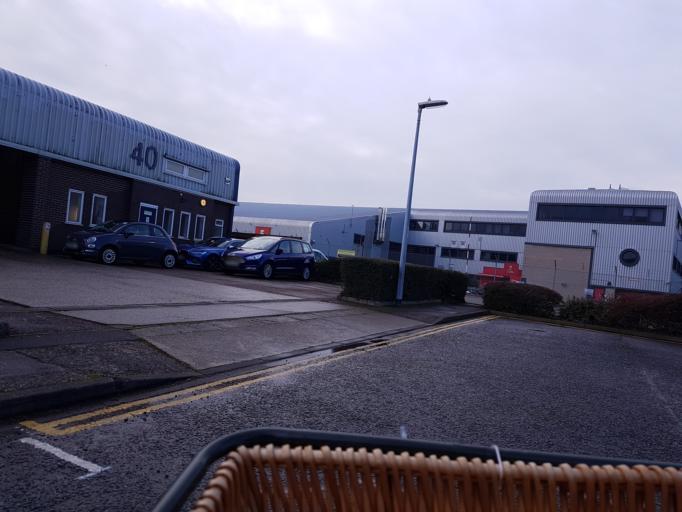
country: GB
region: England
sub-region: Cambridgeshire
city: Cambridge
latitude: 52.1926
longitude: 0.1388
